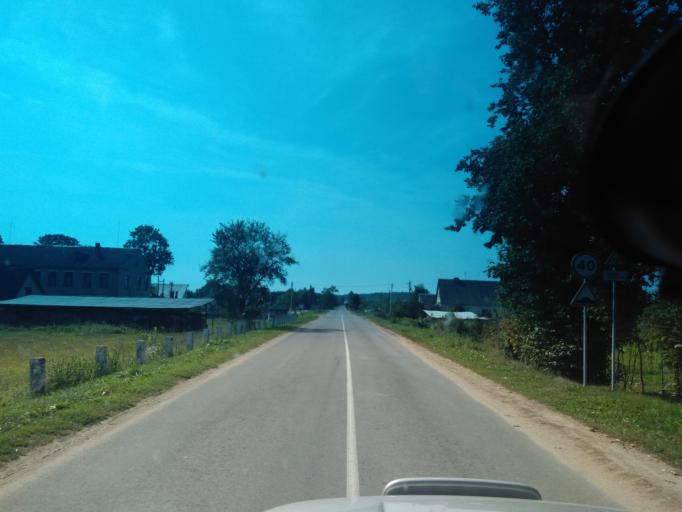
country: BY
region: Minsk
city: Kapyl'
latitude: 53.2080
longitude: 27.1222
